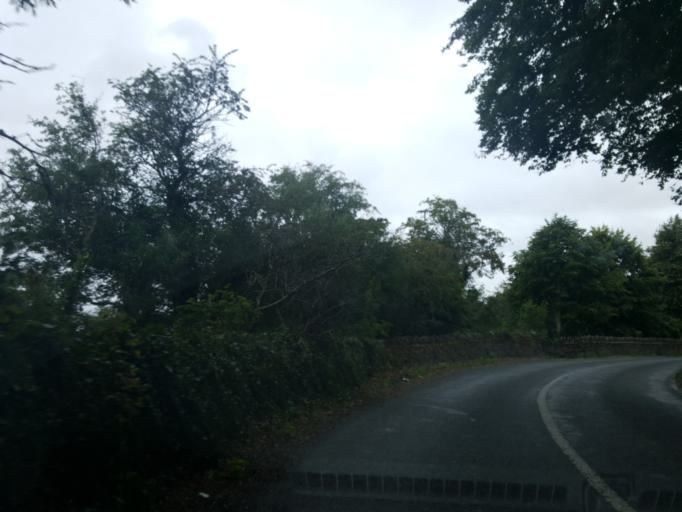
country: IE
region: Leinster
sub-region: Wicklow
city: Valleymount
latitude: 53.1218
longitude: -6.6400
